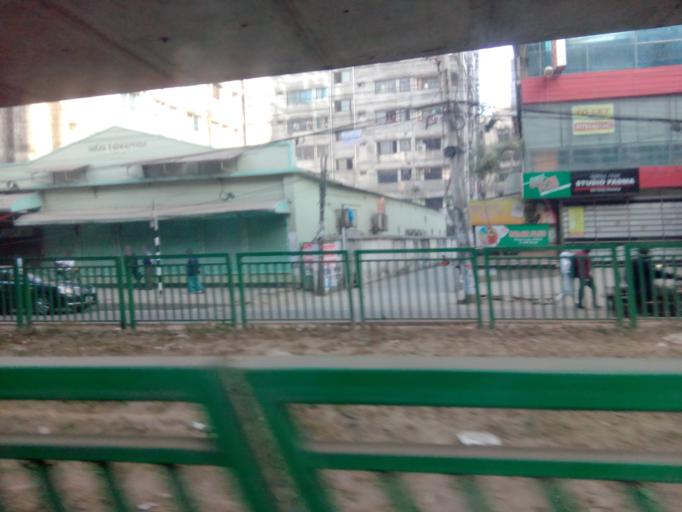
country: BD
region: Dhaka
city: Paltan
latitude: 23.7483
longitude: 90.4021
